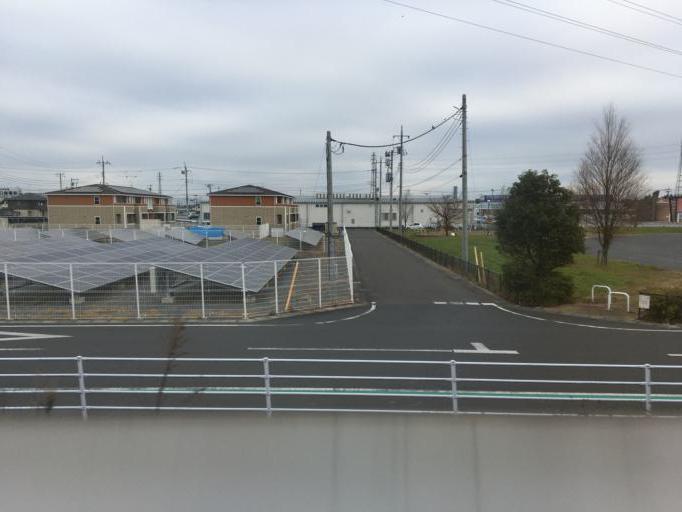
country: JP
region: Tochigi
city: Tochigi
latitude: 36.3512
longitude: 139.7064
